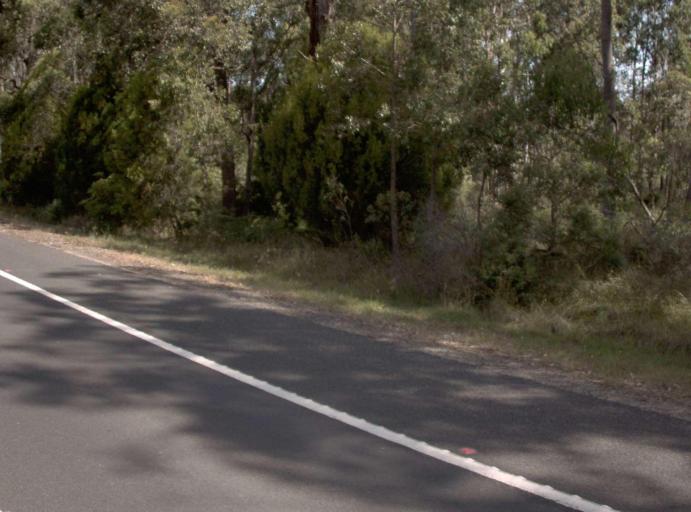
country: AU
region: Victoria
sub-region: East Gippsland
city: Lakes Entrance
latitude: -37.8370
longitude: 147.9198
